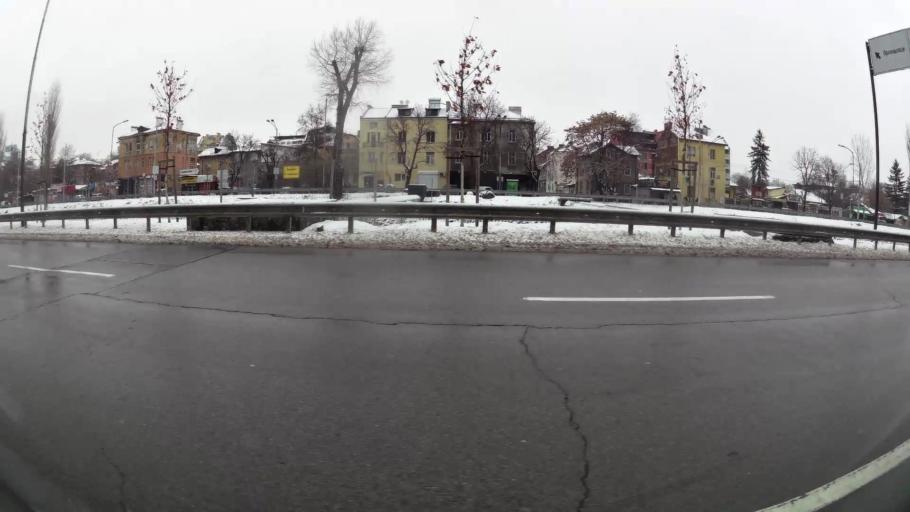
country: BG
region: Sofia-Capital
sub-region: Stolichna Obshtina
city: Sofia
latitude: 42.7045
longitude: 23.3308
